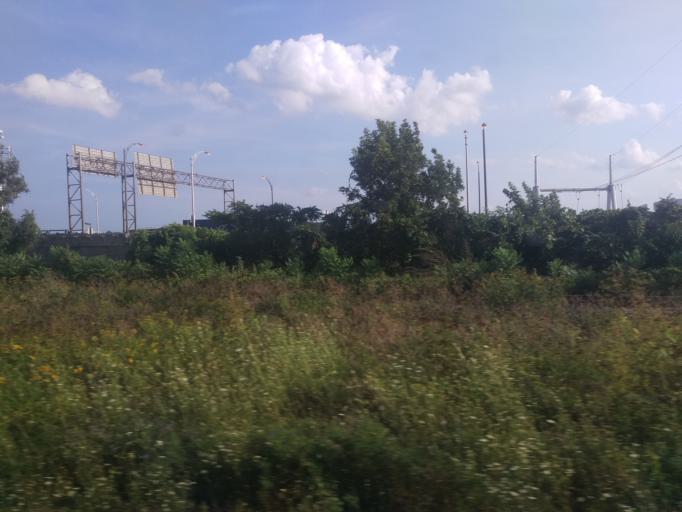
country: CA
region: Quebec
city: Westmount
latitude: 45.4754
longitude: -73.5708
